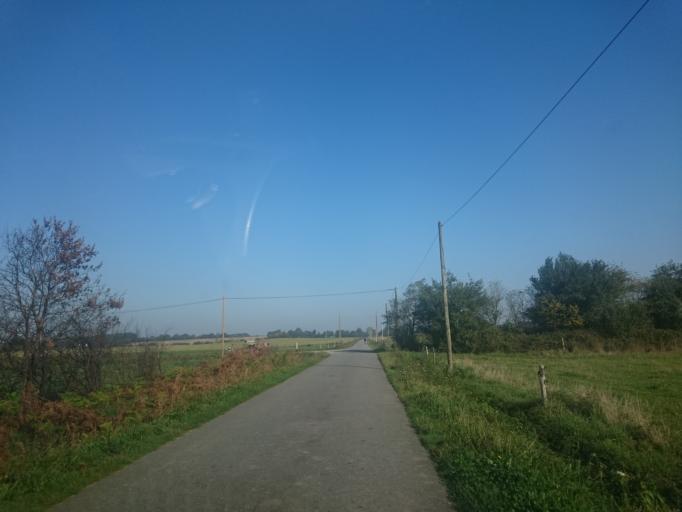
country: FR
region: Brittany
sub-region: Departement d'Ille-et-Vilaine
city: Corps-Nuds
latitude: 47.9421
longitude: -1.5839
